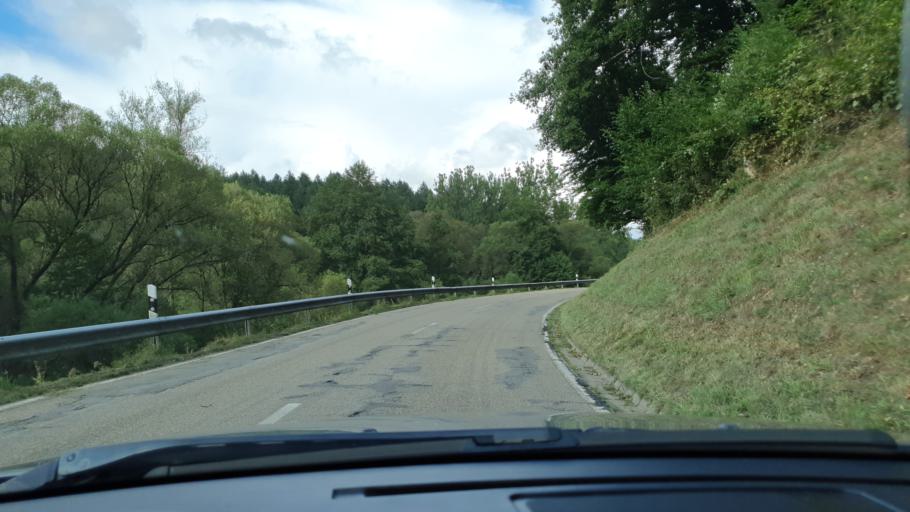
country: DE
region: Rheinland-Pfalz
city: Massweiler
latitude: 49.2625
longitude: 7.5447
